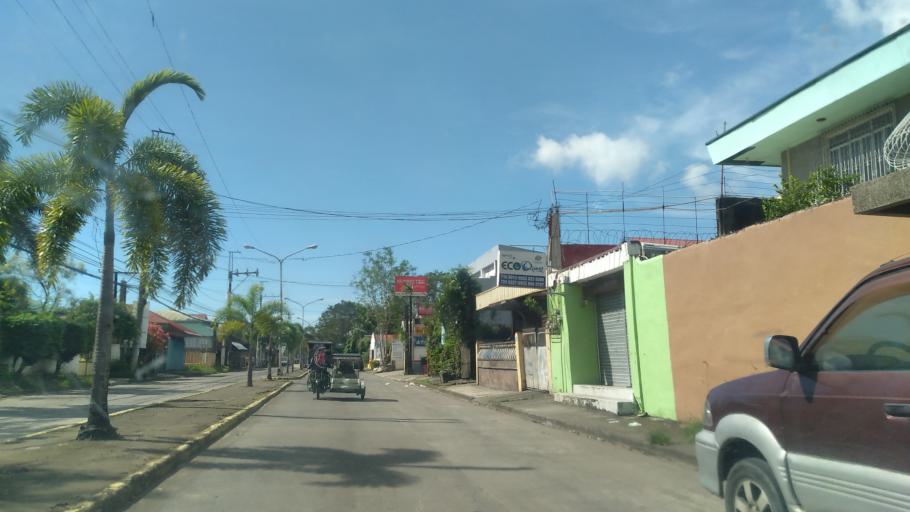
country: PH
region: Calabarzon
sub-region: Province of Quezon
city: Lucena
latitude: 13.9394
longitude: 121.6021
